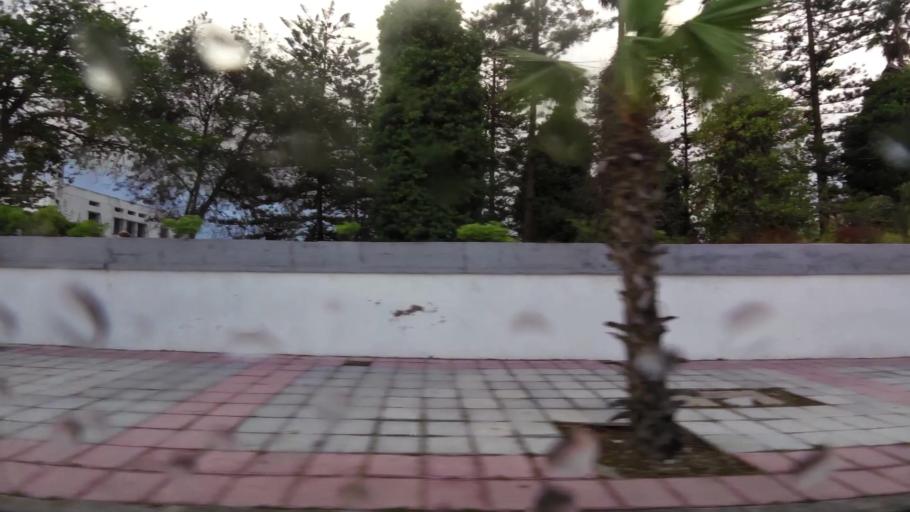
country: MA
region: Doukkala-Abda
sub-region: El-Jadida
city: El Jadida
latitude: 33.2456
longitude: -8.5062
